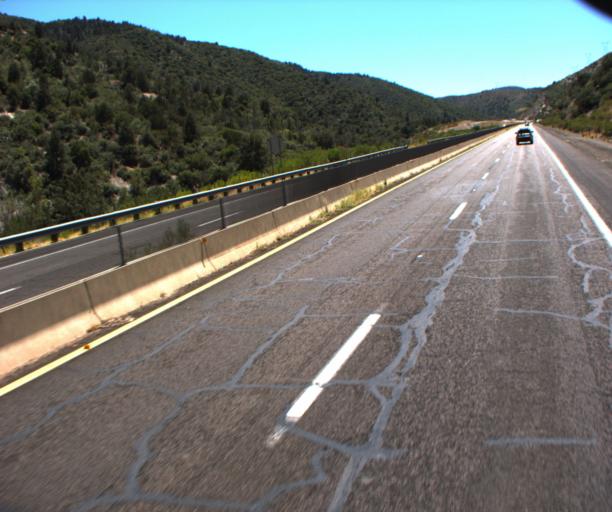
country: US
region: Arizona
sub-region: Gila County
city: Tonto Basin
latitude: 33.9530
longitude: -111.4123
